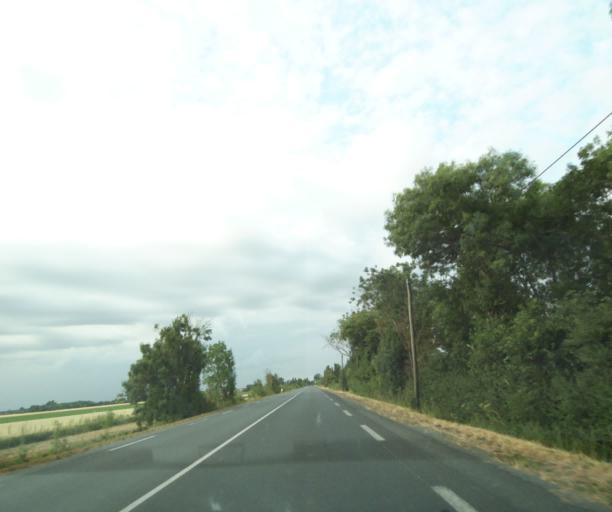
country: FR
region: Pays de la Loire
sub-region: Departement de la Vendee
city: Chaille-les-Marais
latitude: 46.3582
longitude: -0.9915
